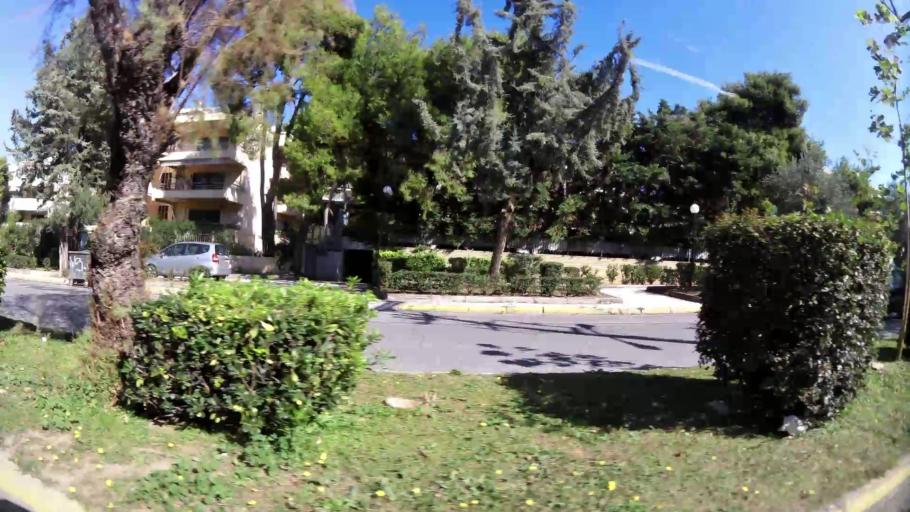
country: GR
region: Attica
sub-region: Nomarchia Athinas
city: Kifisia
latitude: 38.0880
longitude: 23.7994
